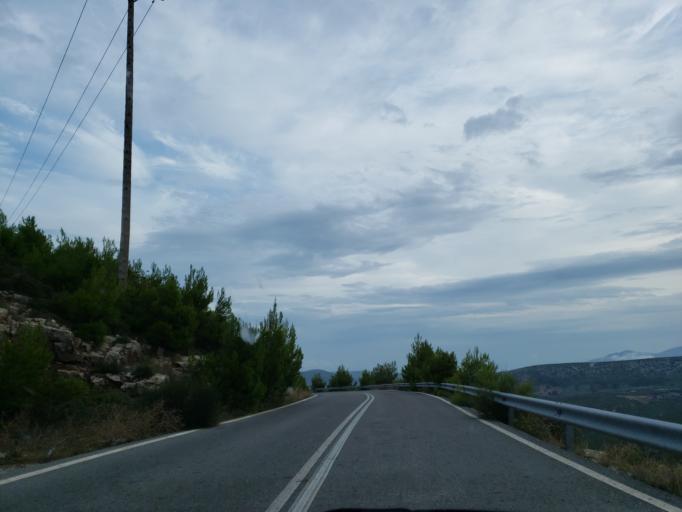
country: GR
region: Attica
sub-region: Nomarchia Anatolikis Attikis
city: Grammatiko
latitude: 38.2087
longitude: 23.9492
